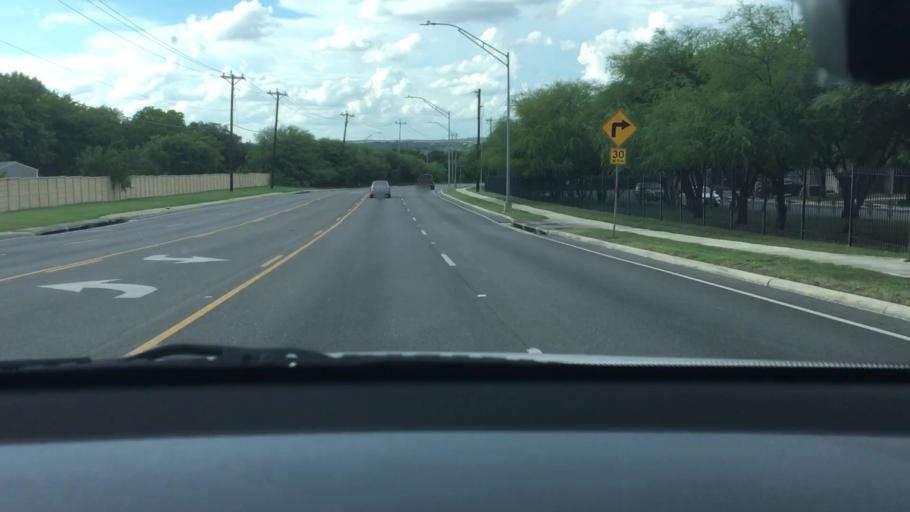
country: US
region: Texas
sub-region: Bexar County
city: Live Oak
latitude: 29.5981
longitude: -98.4040
